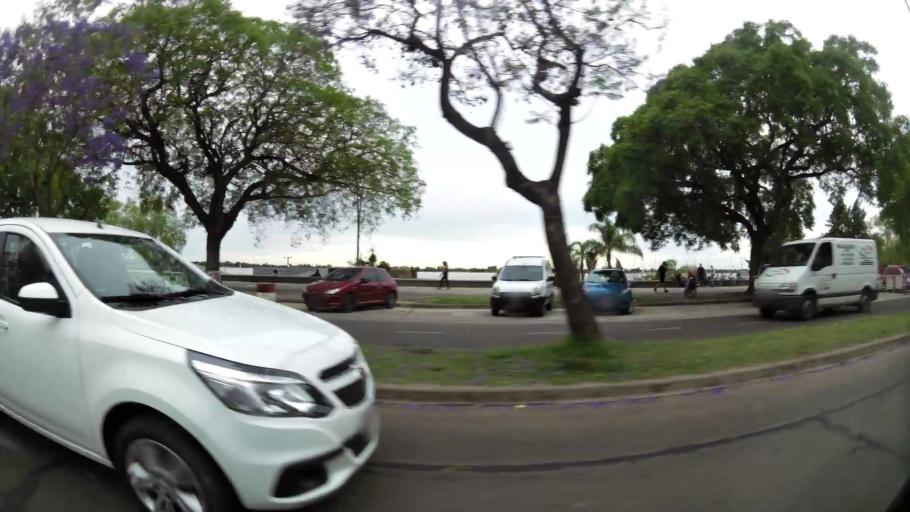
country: AR
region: Santa Fe
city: Granadero Baigorria
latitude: -32.8920
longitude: -60.6859
